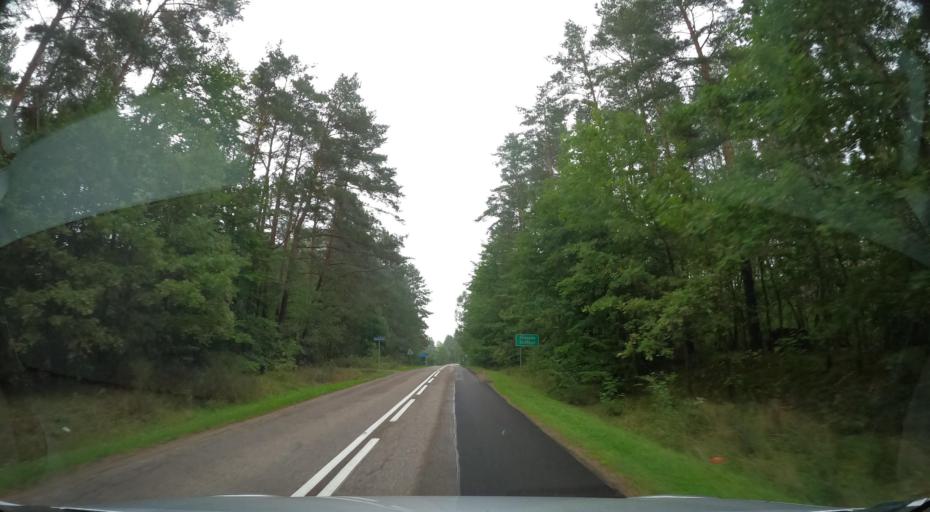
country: PL
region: Pomeranian Voivodeship
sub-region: Powiat wejherowski
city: Linia
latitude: 54.4659
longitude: 17.9858
